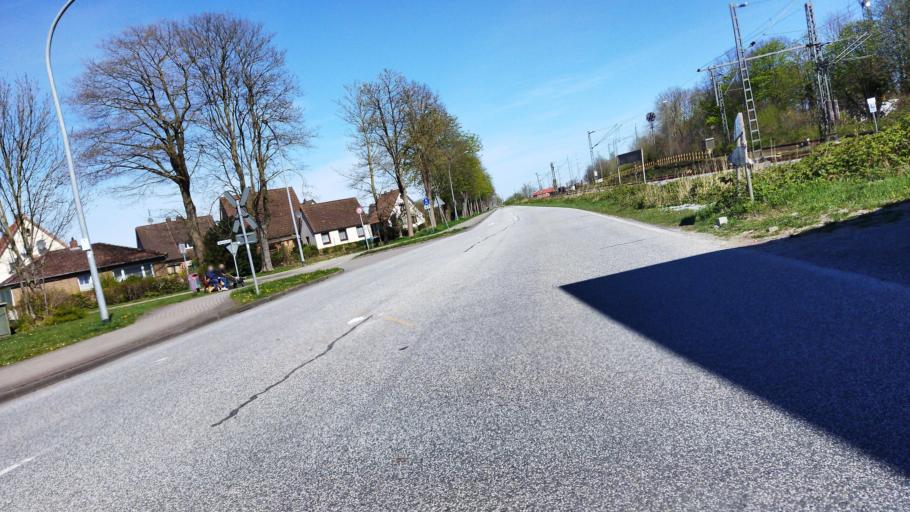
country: DE
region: Lower Saxony
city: Brake (Unterweser)
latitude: 53.3390
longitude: 8.4796
